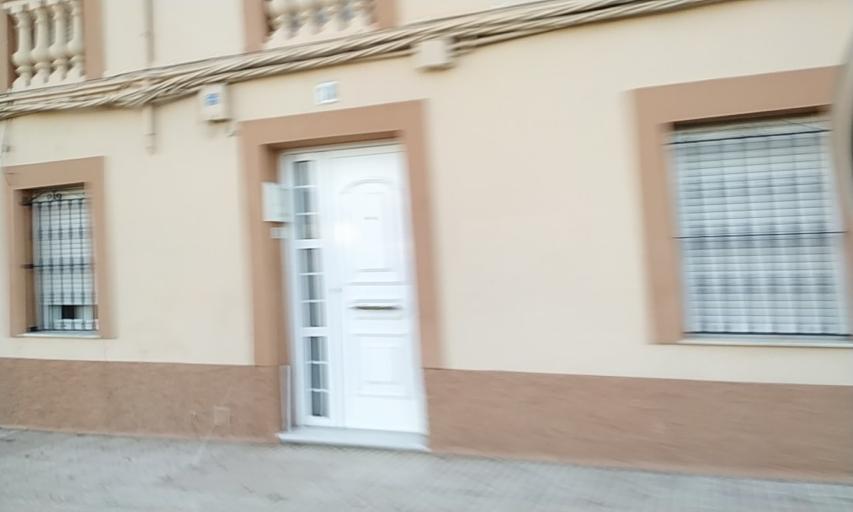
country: ES
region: Extremadura
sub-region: Provincia de Caceres
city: Valencia de Alcantara
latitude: 39.4082
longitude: -7.2421
